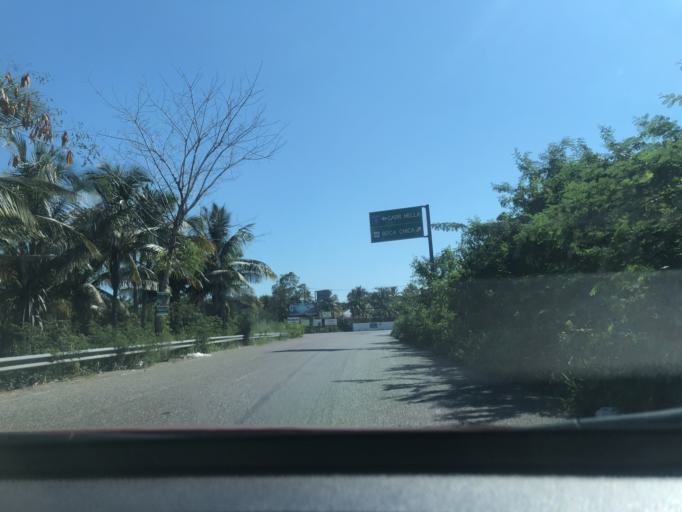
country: DO
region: Santo Domingo
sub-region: Santo Domingo
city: Boca Chica
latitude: 18.4505
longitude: -69.5971
